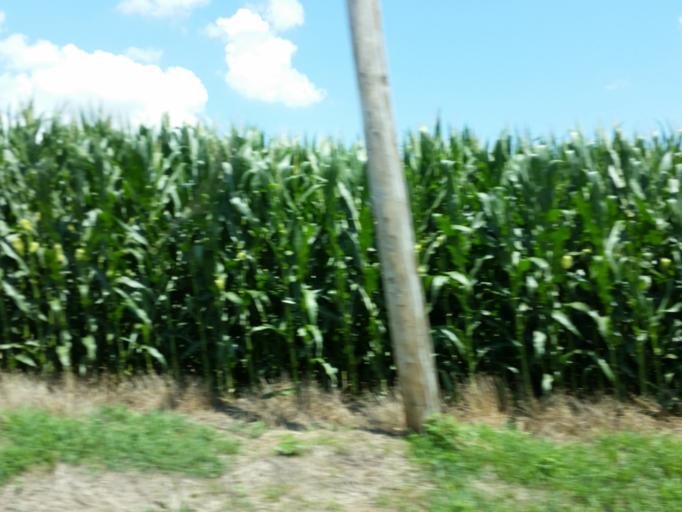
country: US
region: Kentucky
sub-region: Fulton County
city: Hickman
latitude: 36.5582
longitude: -89.2863
